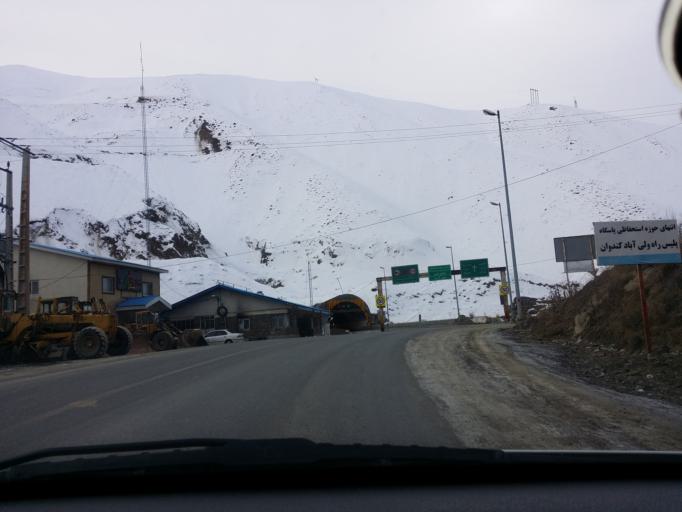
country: IR
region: Tehran
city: Tajrish
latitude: 36.1612
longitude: 51.3160
